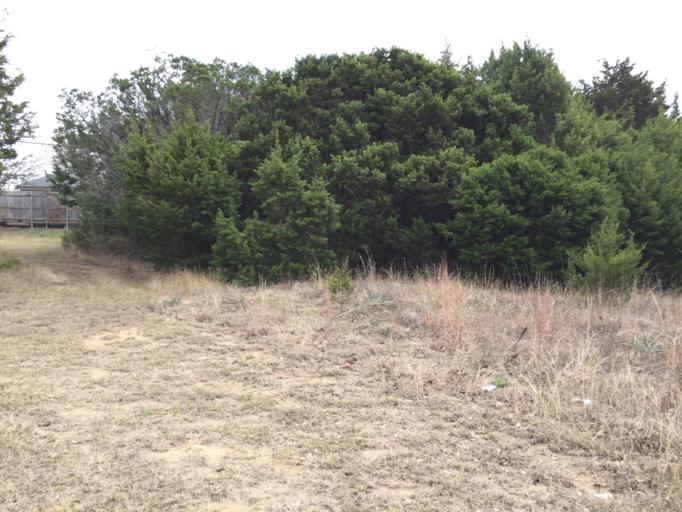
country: US
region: Texas
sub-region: Bell County
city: Harker Heights
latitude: 31.0693
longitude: -97.6609
